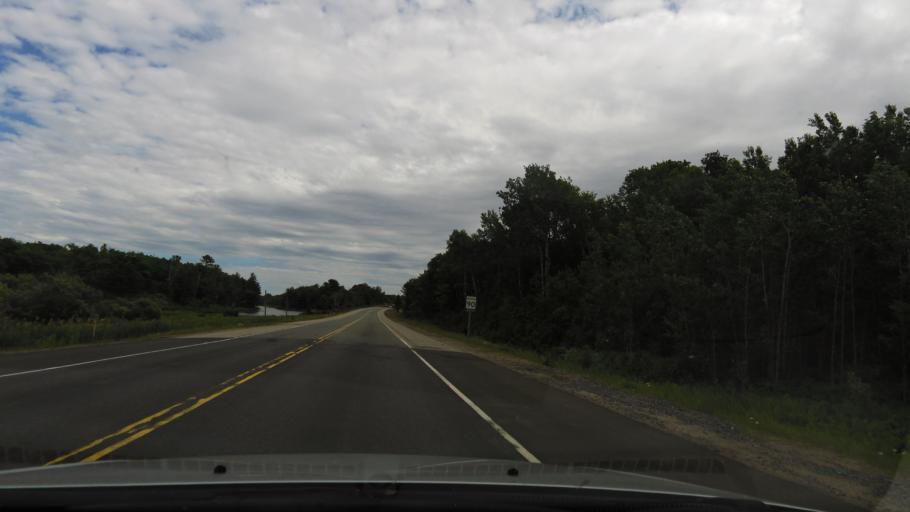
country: CA
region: Ontario
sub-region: Parry Sound District
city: Parry Sound
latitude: 45.5472
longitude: -80.2790
